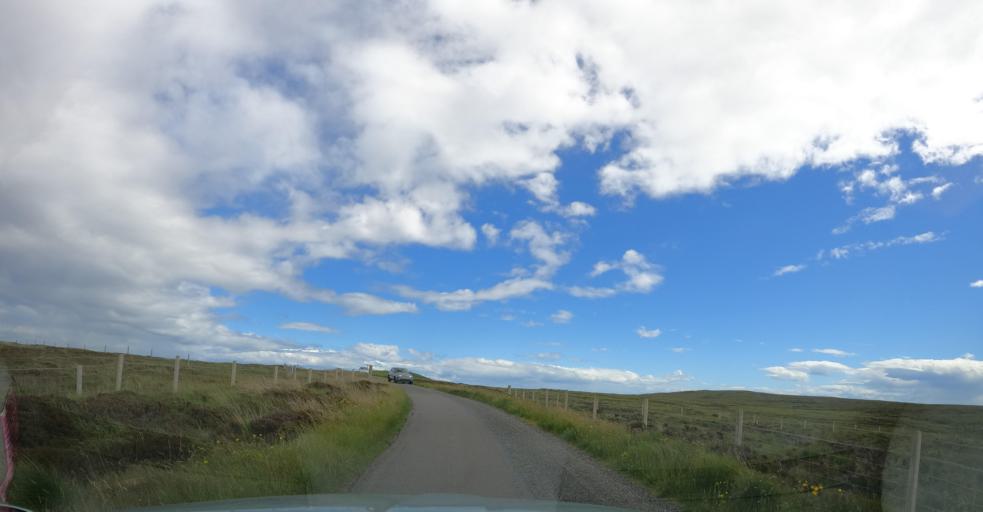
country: GB
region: Scotland
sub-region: Eilean Siar
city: Stornoway
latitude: 58.2048
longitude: -6.2463
